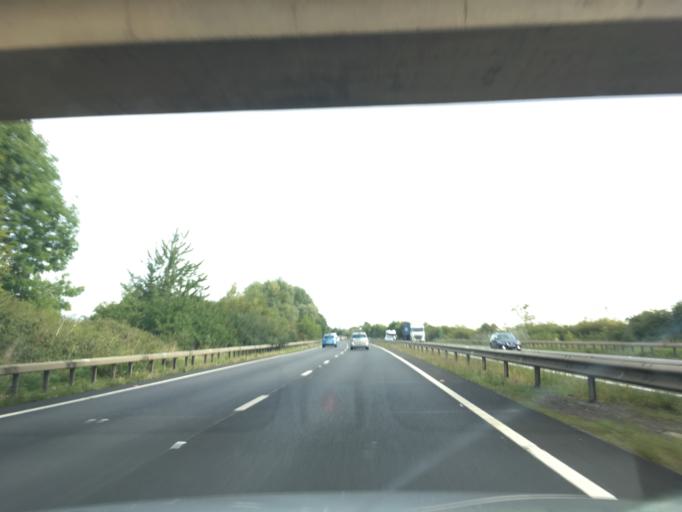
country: GB
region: England
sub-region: Oxfordshire
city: Kidlington
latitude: 51.8154
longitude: -1.2653
